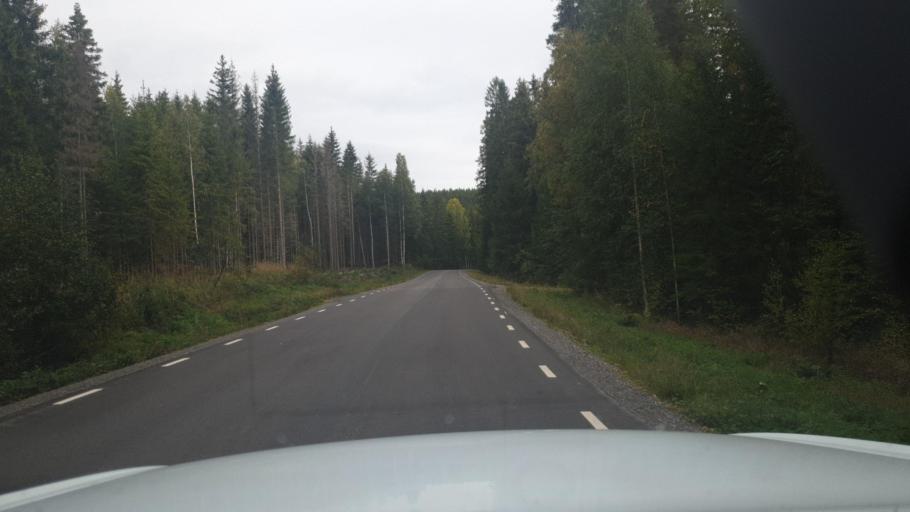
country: SE
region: Vaermland
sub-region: Torsby Kommun
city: Torsby
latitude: 60.0014
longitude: 12.7298
